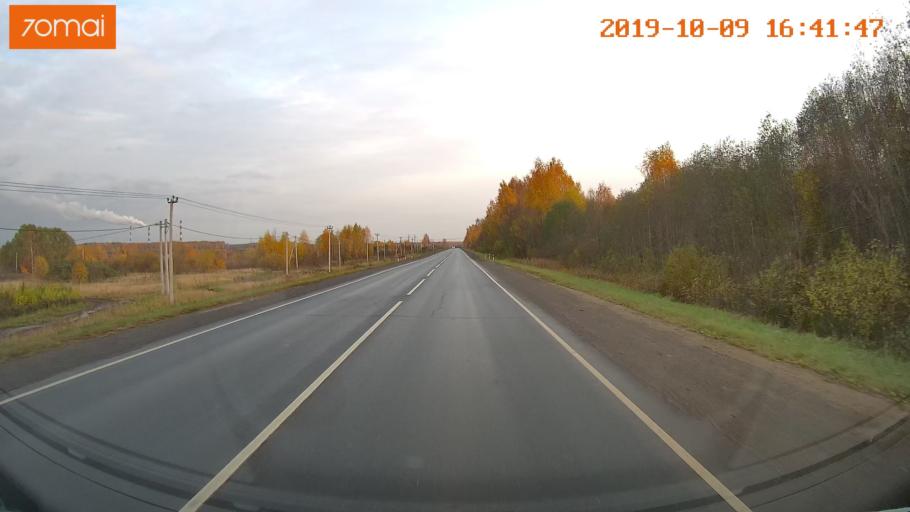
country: RU
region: Kostroma
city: Volgorechensk
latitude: 57.4693
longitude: 41.0877
